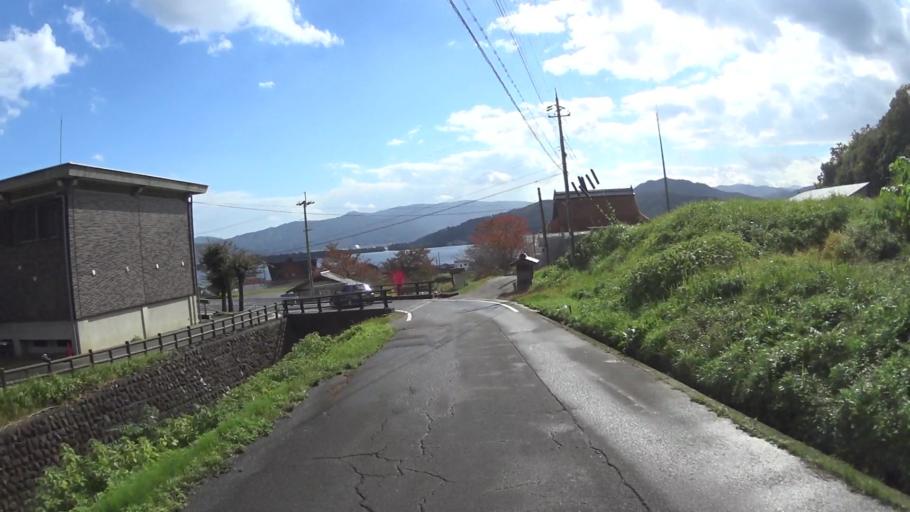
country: JP
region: Kyoto
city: Miyazu
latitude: 35.5801
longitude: 135.1779
